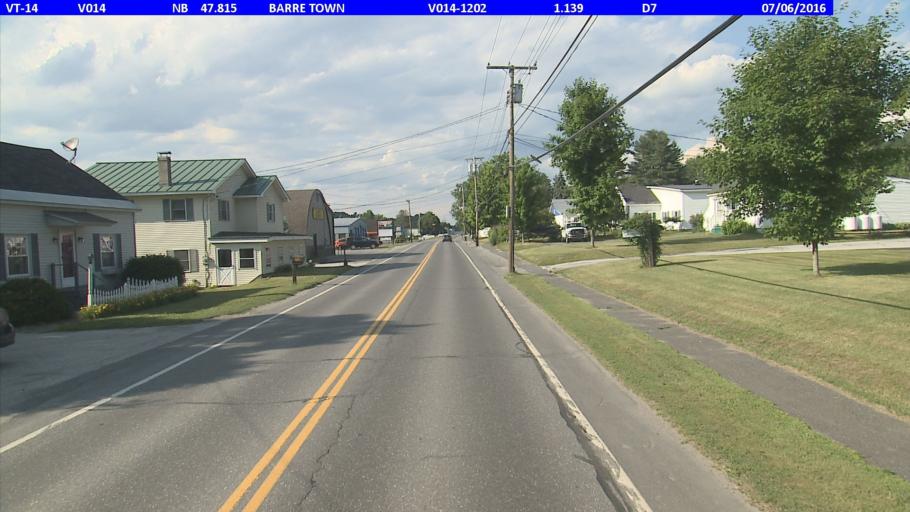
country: US
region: Vermont
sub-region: Washington County
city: South Barre
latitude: 44.1658
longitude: -72.5108
